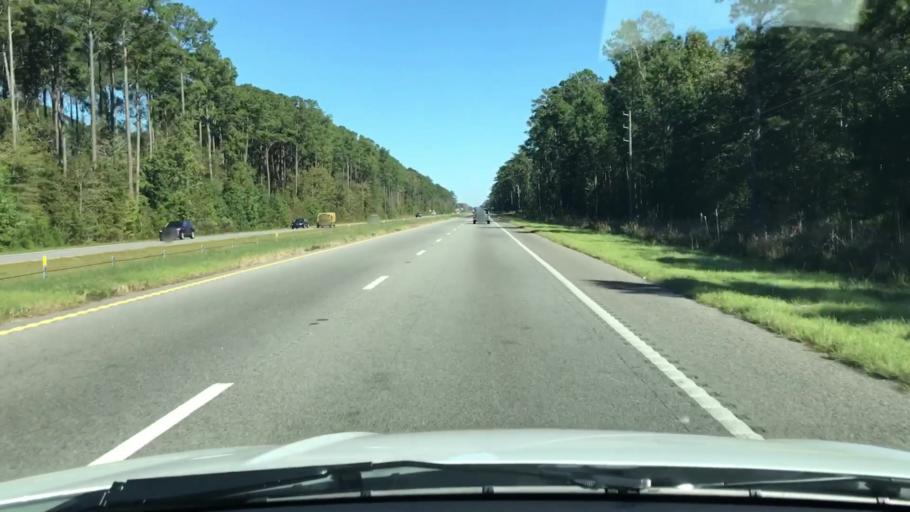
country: US
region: South Carolina
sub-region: Colleton County
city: Walterboro
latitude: 32.7636
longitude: -80.5132
